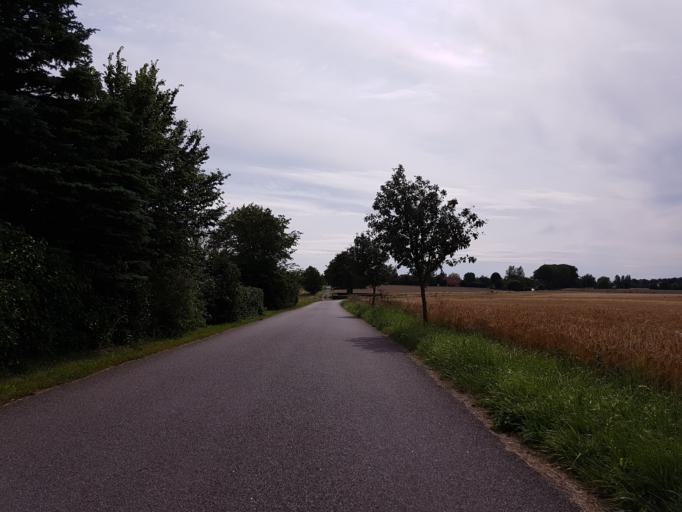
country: DK
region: Zealand
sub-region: Guldborgsund Kommune
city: Nykobing Falster
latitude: 54.5829
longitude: 11.9452
